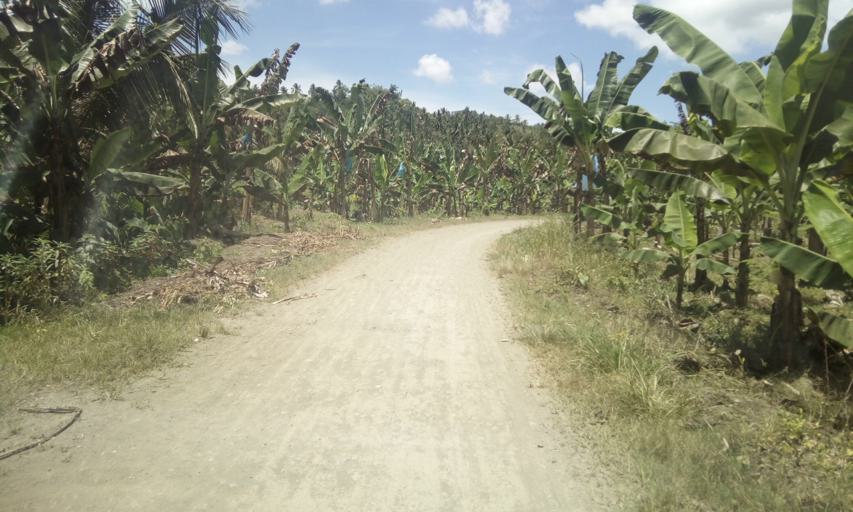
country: PH
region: Caraga
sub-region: Province of Agusan del Sur
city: Santa Josefa
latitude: 7.9537
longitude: 125.9971
